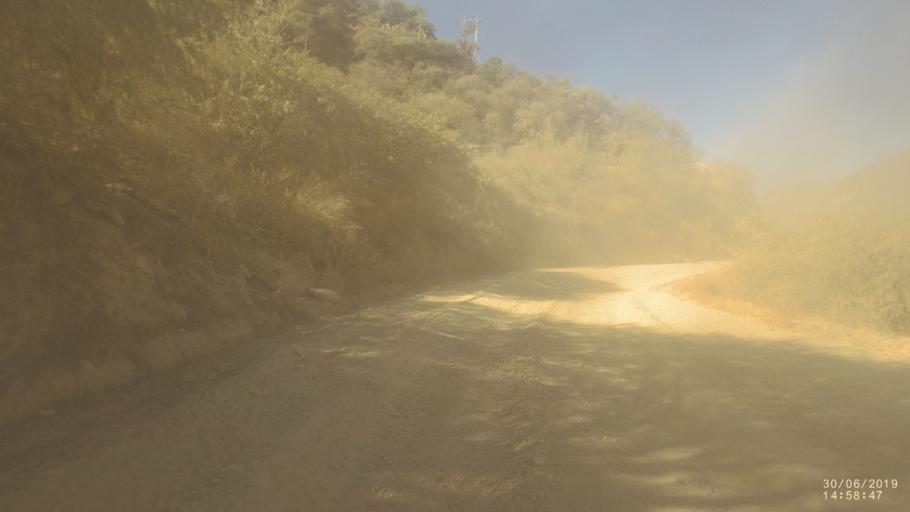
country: BO
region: Cochabamba
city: Irpa Irpa
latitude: -17.7379
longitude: -66.3478
